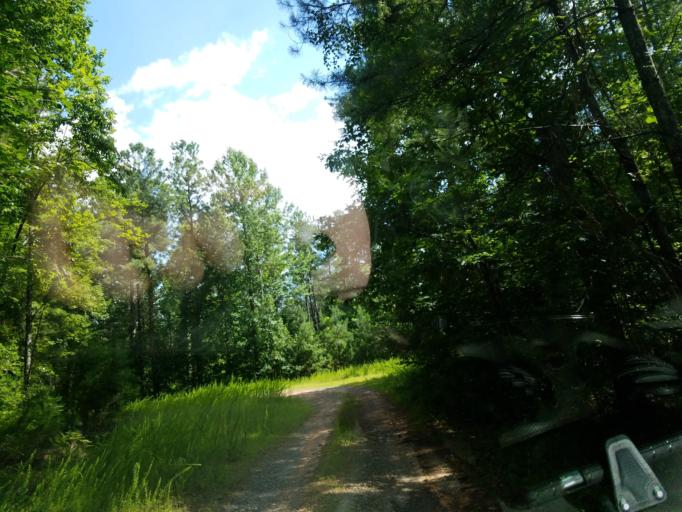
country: US
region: Georgia
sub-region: Lumpkin County
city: Dahlonega
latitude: 34.5638
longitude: -84.1232
